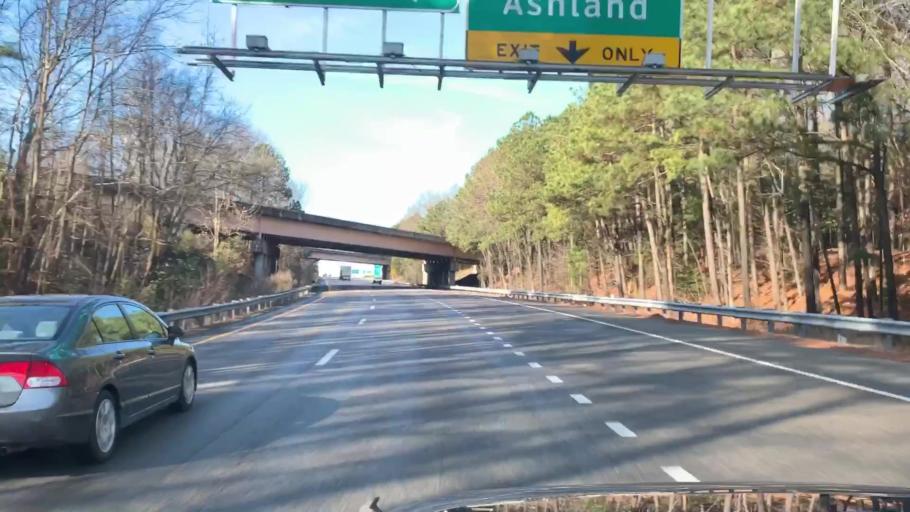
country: US
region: Virginia
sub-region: Henrico County
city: Chamberlayne
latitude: 37.6570
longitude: -77.4429
